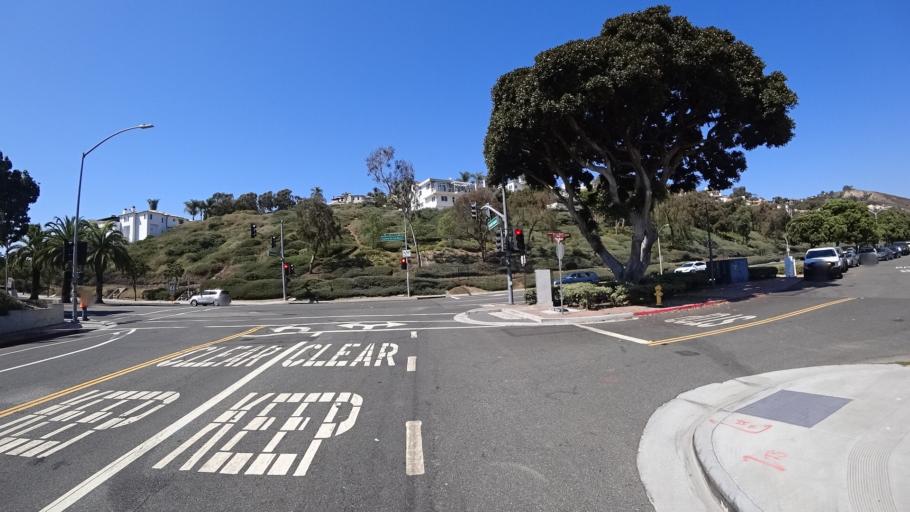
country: US
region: California
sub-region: Orange County
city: San Clemente
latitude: 33.4576
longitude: -117.6435
